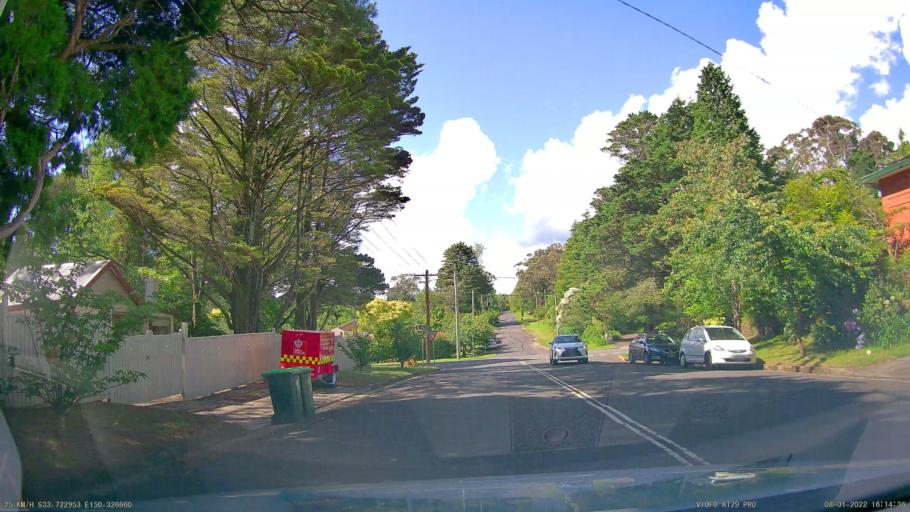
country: AU
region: New South Wales
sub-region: Blue Mountains Municipality
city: Leura
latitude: -33.7229
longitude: 150.3267
